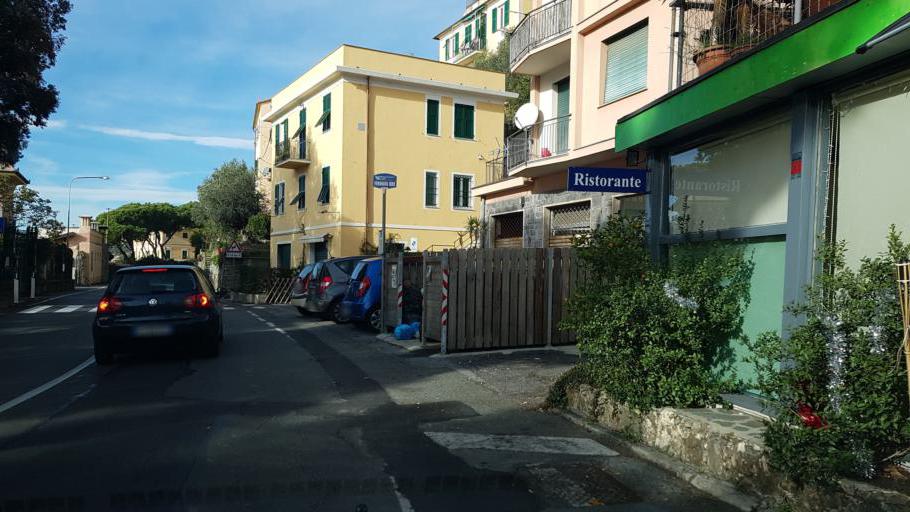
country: IT
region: Liguria
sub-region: Provincia di Genova
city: Sori
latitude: 44.3669
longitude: 9.1168
